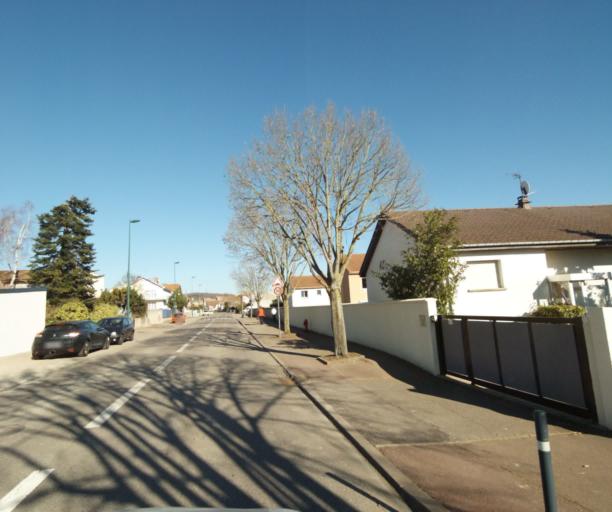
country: FR
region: Lorraine
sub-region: Departement de Meurthe-et-Moselle
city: Saulxures-les-Nancy
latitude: 48.6861
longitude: 6.2415
